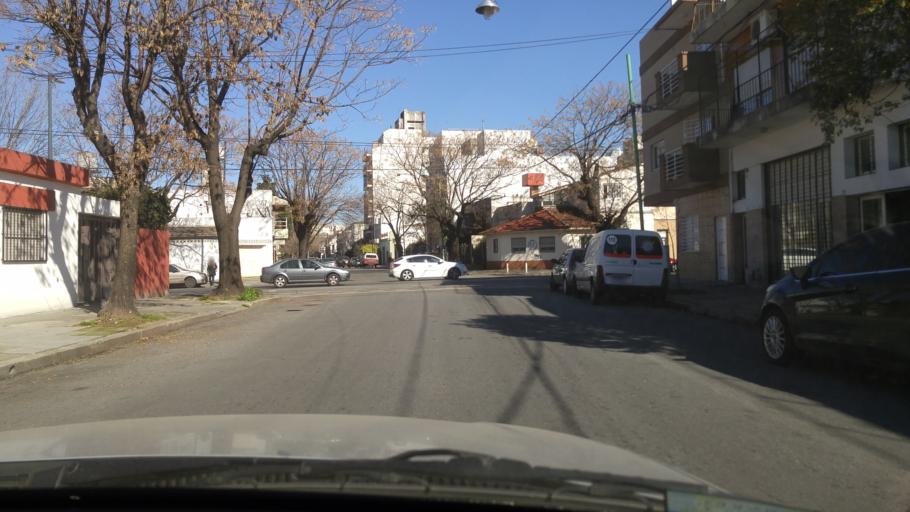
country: AR
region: Buenos Aires F.D.
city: Villa Santa Rita
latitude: -34.6204
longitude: -58.4823
